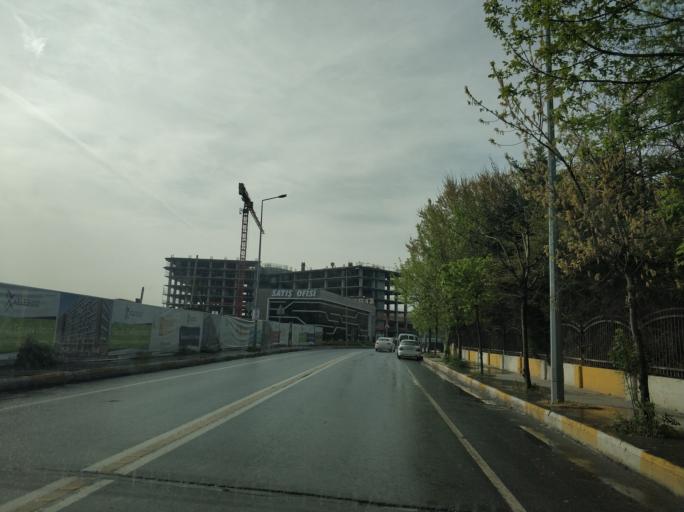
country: TR
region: Istanbul
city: Bahcelievler
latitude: 41.0018
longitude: 28.8095
